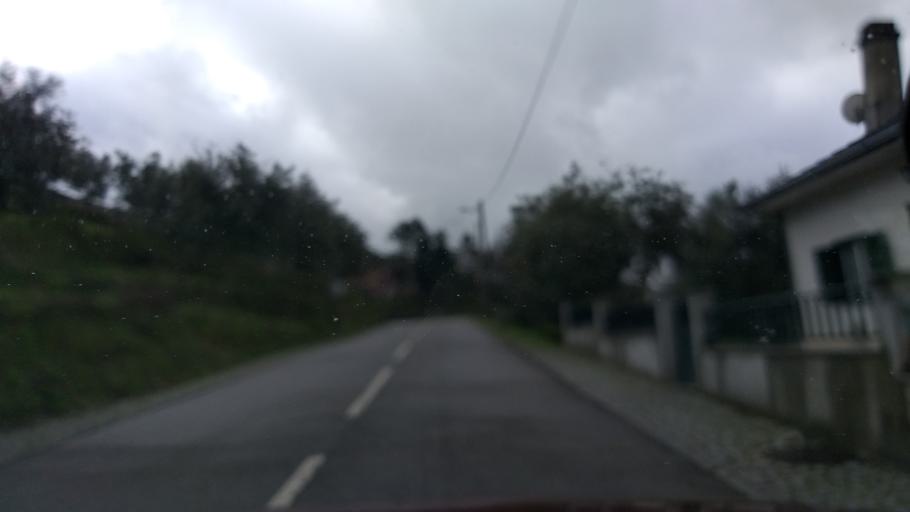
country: PT
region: Guarda
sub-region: Celorico da Beira
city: Celorico da Beira
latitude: 40.7079
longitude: -7.4310
